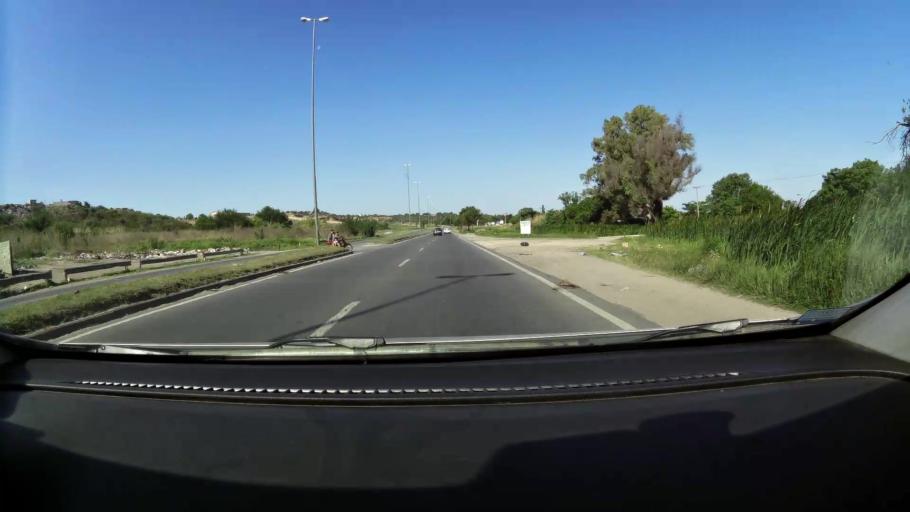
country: AR
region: Cordoba
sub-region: Departamento de Capital
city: Cordoba
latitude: -31.4006
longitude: -64.1471
